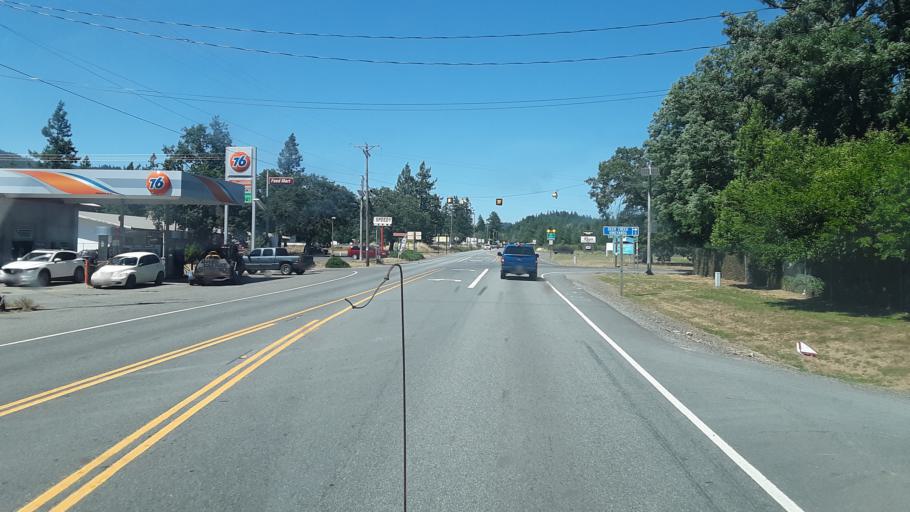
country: US
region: Oregon
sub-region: Josephine County
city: Cave Junction
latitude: 42.2785
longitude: -123.6163
